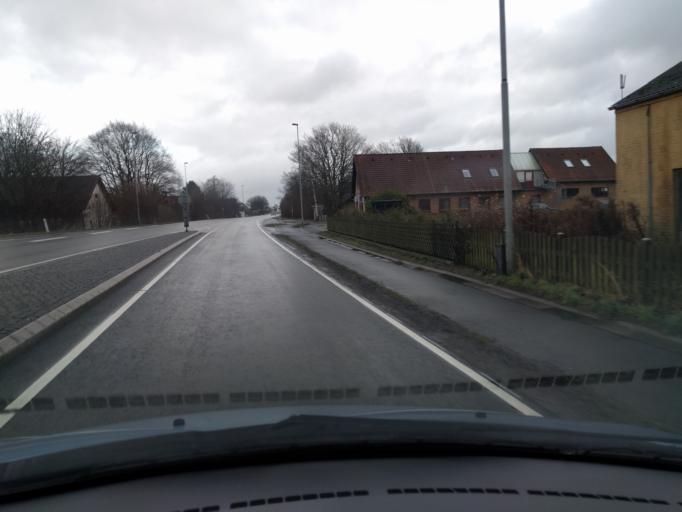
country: DK
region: South Denmark
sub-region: Kerteminde Kommune
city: Langeskov
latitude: 55.3853
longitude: 10.5266
